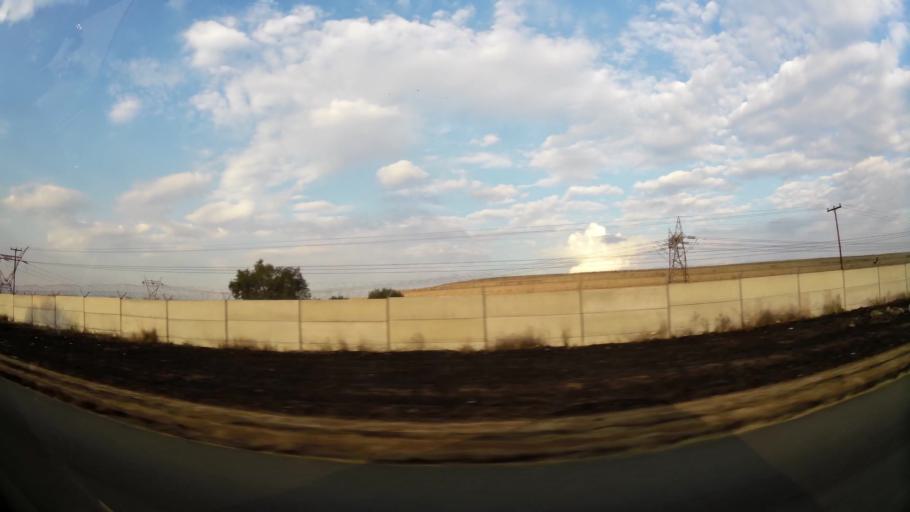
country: ZA
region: Gauteng
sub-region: Sedibeng District Municipality
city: Vanderbijlpark
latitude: -26.6341
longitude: 27.8078
